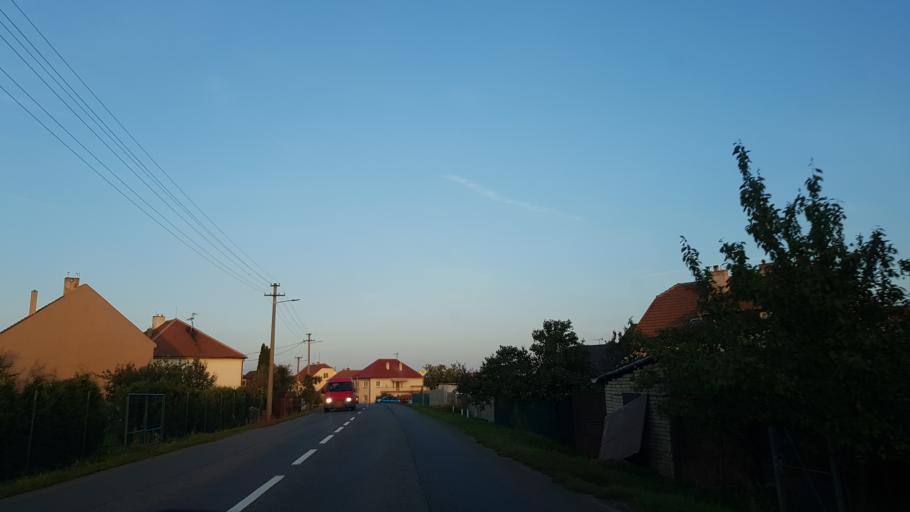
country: CZ
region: Zlin
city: Nedakonice
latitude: 49.0298
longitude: 17.3738
